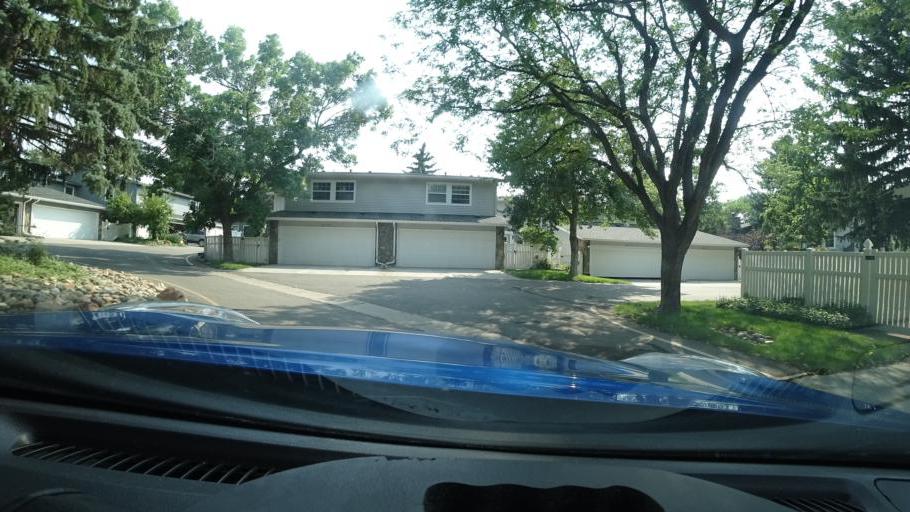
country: US
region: Colorado
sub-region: Adams County
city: Aurora
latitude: 39.6652
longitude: -104.8341
